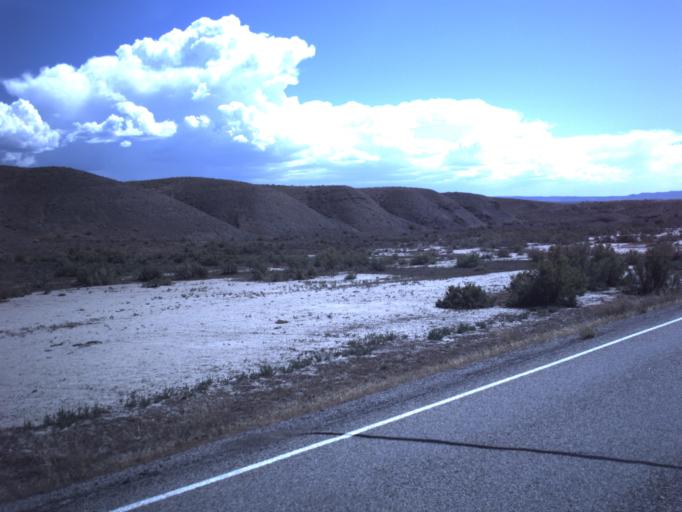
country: US
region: Utah
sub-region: Grand County
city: Moab
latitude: 38.8782
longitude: -109.3088
